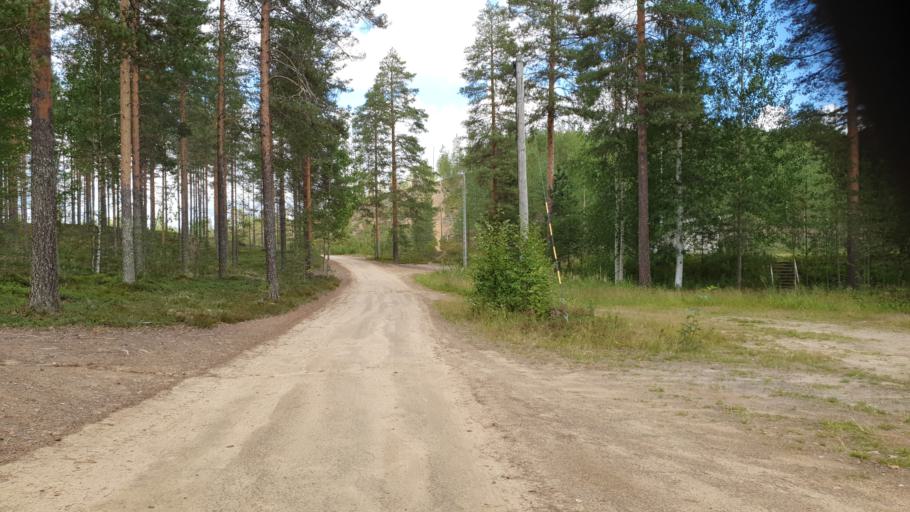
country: FI
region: Kainuu
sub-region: Kehys-Kainuu
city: Kuhmo
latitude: 64.1509
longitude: 29.3883
